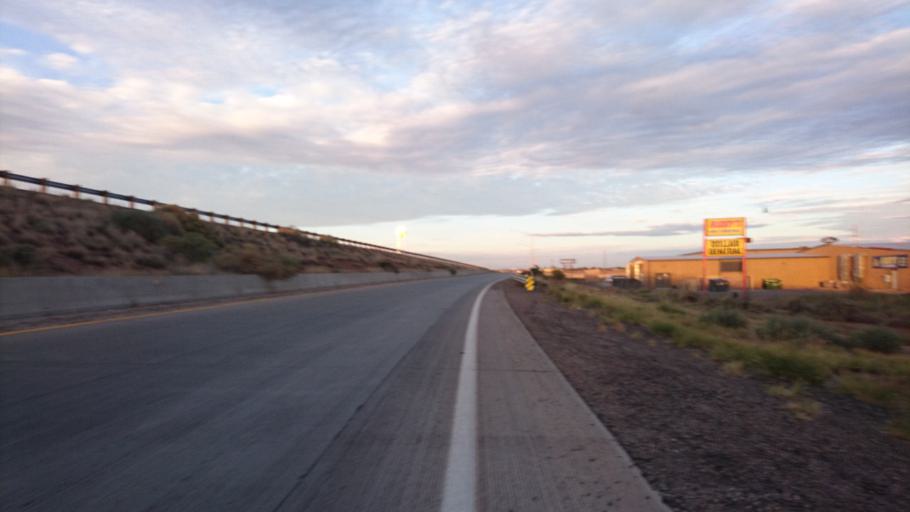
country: US
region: Arizona
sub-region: Navajo County
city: Winslow
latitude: 35.0399
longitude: -110.7001
